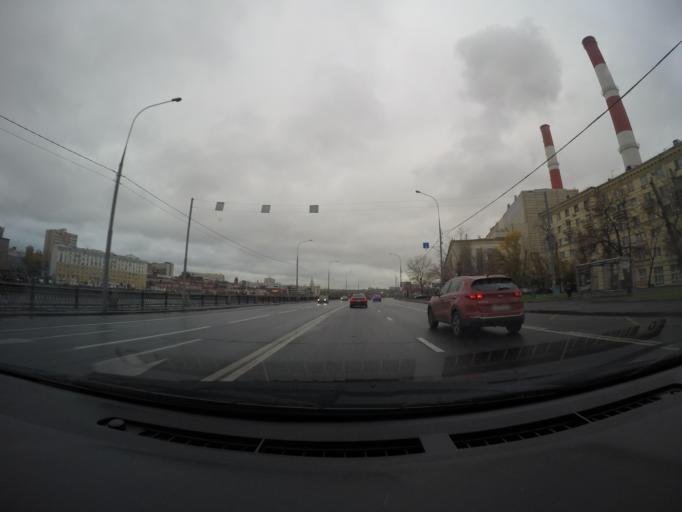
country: RU
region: Moskovskaya
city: Dorogomilovo
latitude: 55.7369
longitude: 37.5641
